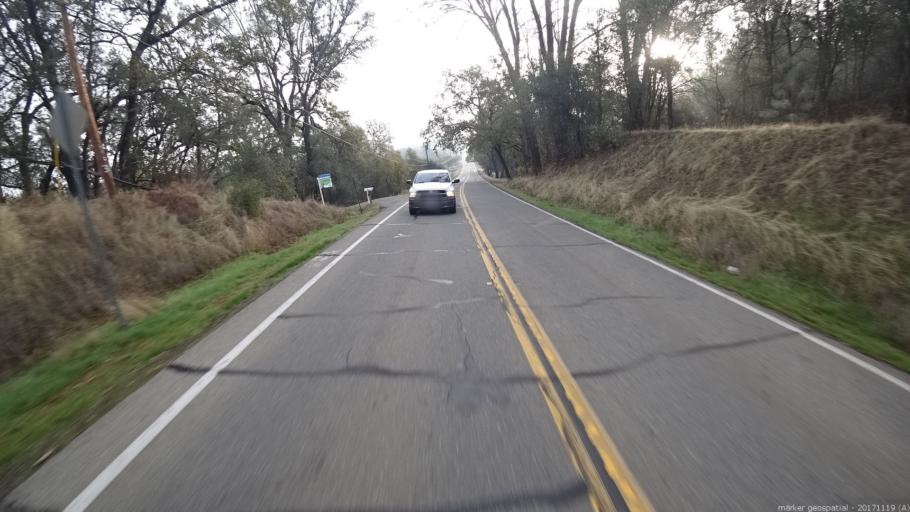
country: US
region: California
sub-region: Shasta County
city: Anderson
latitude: 40.4804
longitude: -122.2633
